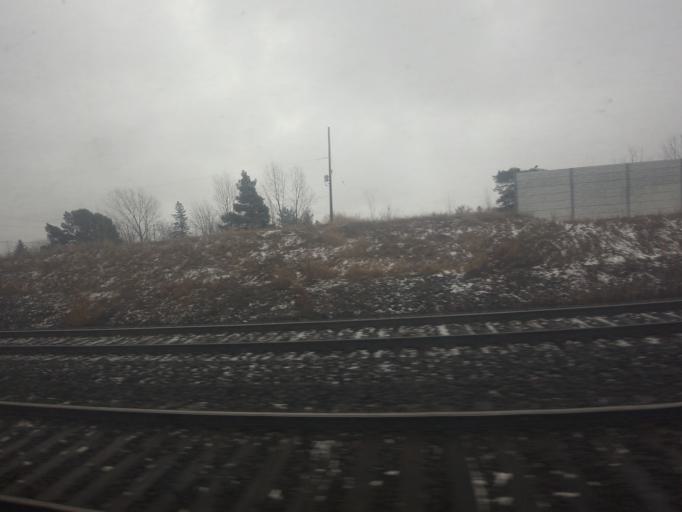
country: CA
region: Ontario
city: Belleville
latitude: 44.1910
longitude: -77.3291
